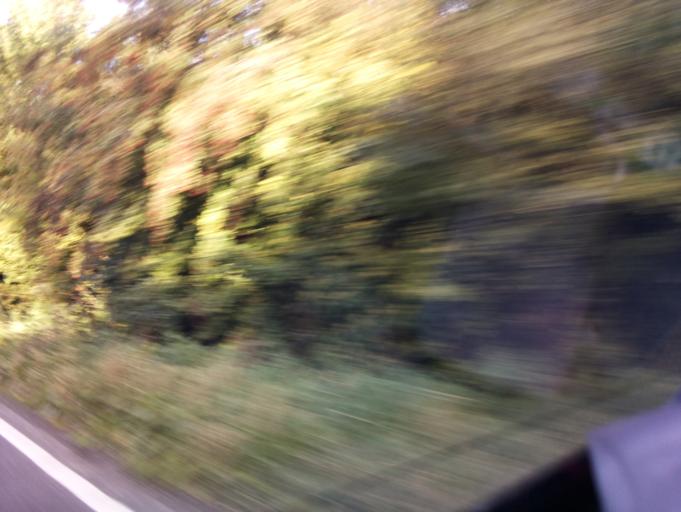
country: GB
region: England
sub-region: Hampshire
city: Swanmore
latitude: 50.9723
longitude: -1.1315
